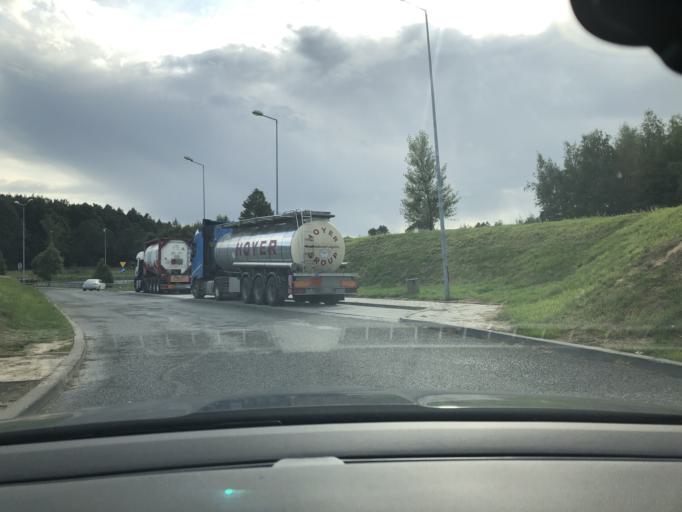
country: PL
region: Opole Voivodeship
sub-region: Powiat strzelecki
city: Lesnica
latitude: 50.4634
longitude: 18.1590
